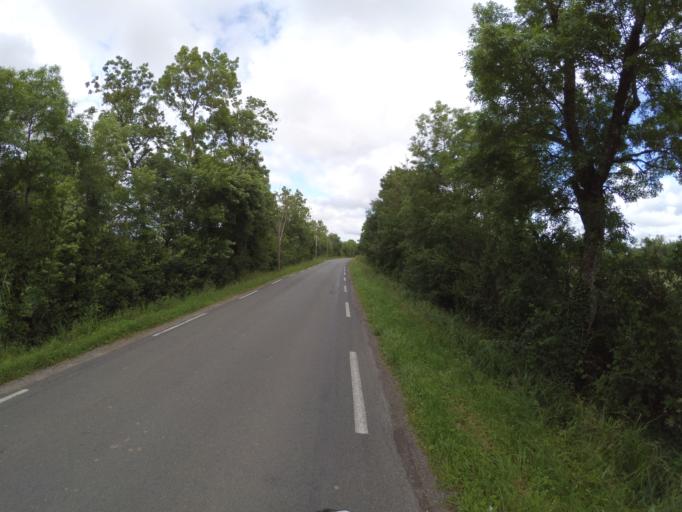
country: FR
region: Aquitaine
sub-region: Departement de la Gironde
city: Ludon-Medoc
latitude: 44.9848
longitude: -0.5725
